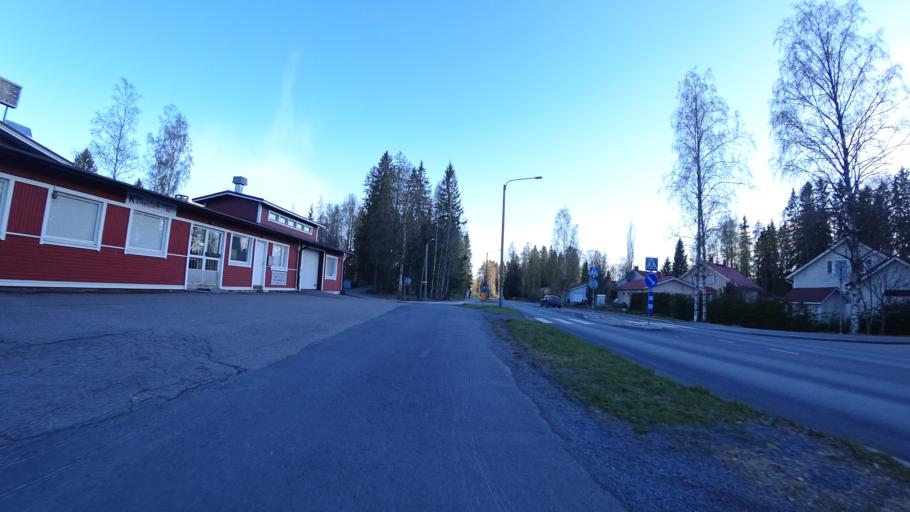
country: FI
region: Pirkanmaa
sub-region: Tampere
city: Yloejaervi
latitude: 61.5120
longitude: 23.5956
